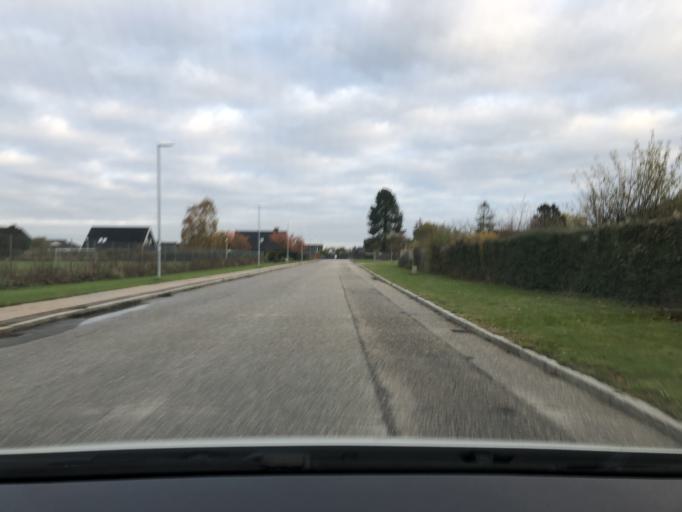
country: DK
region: Capital Region
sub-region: Tarnby Kommune
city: Tarnby
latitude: 55.6054
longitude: 12.5904
